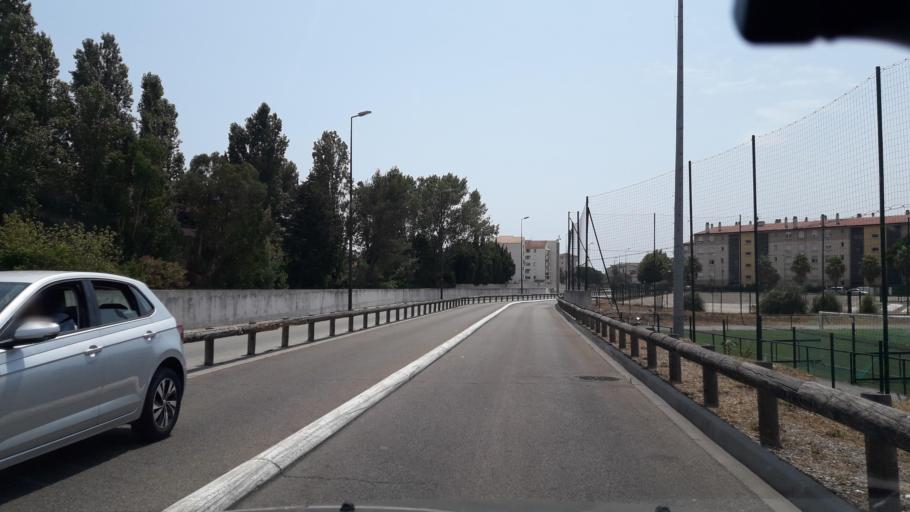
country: FR
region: Provence-Alpes-Cote d'Azur
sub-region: Departement du Var
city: Saint-Raphael
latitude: 43.4321
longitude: 6.7643
